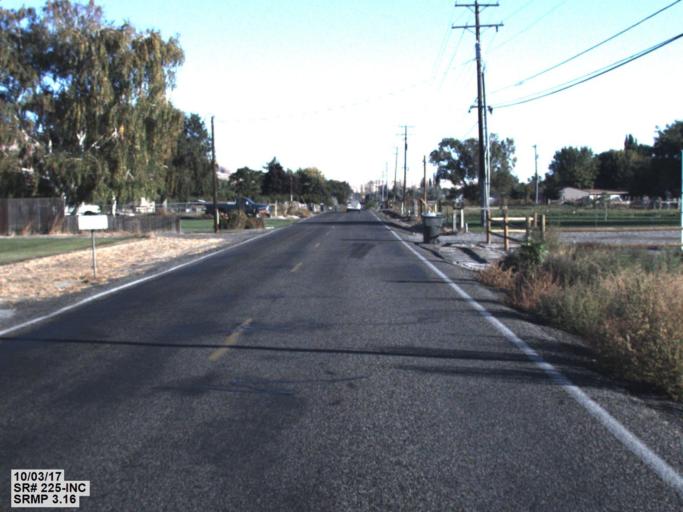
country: US
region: Washington
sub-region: Benton County
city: Benton City
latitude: 46.2890
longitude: -119.4940
